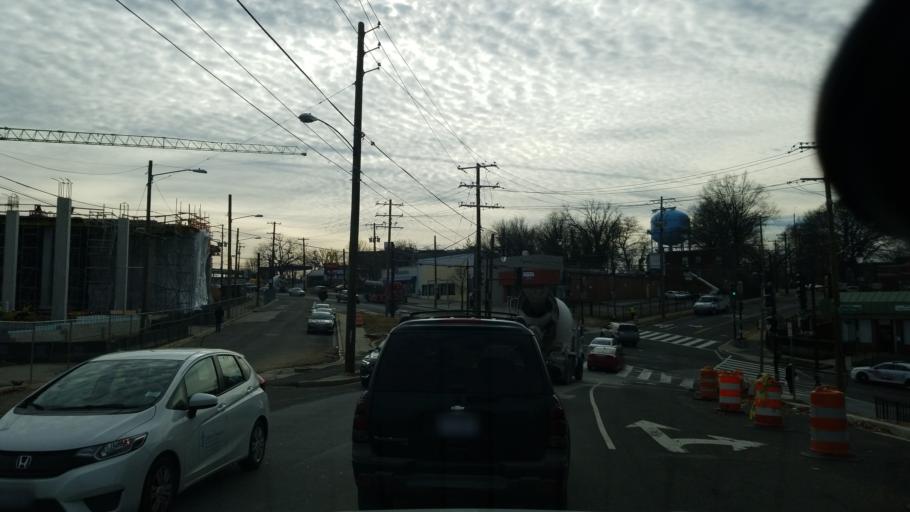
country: US
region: Maryland
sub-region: Prince George's County
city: Hillcrest Heights
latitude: 38.8618
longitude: -76.9693
